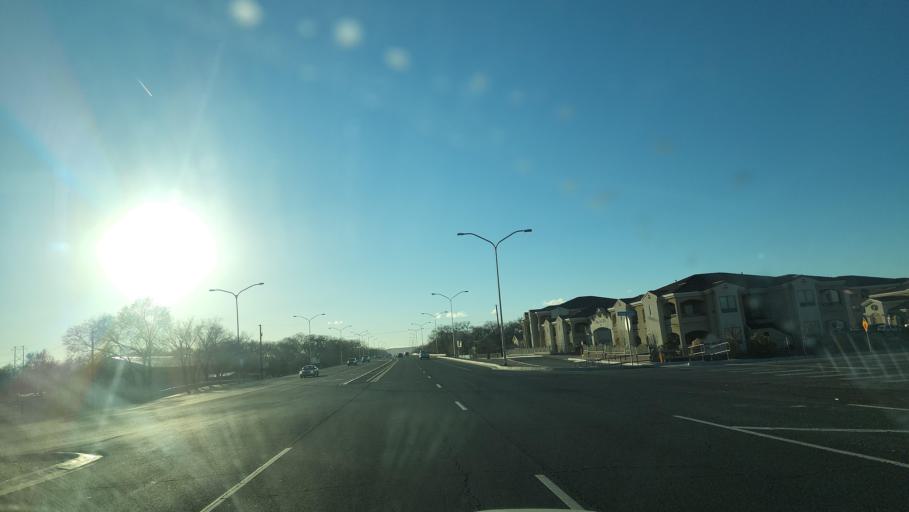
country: US
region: New Mexico
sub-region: Bernalillo County
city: South Valley
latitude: 35.0273
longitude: -106.6656
